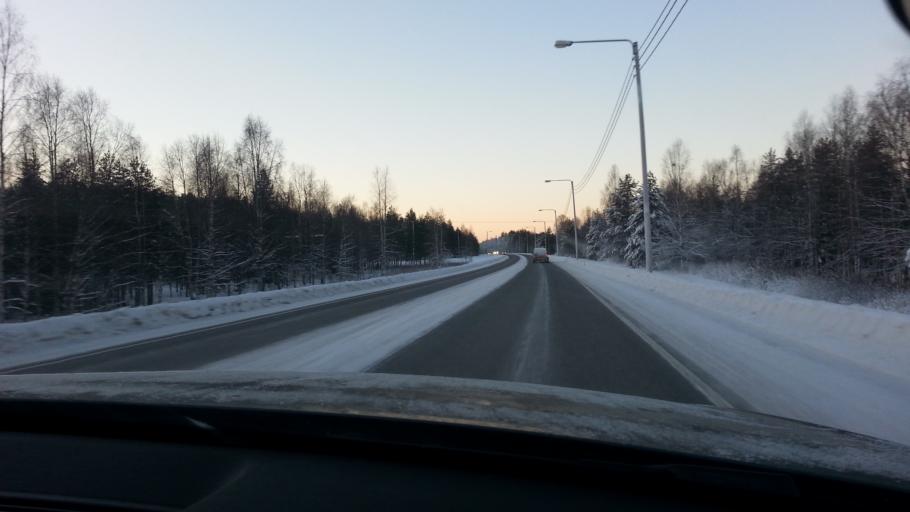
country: FI
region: Lapland
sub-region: Rovaniemi
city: Rovaniemi
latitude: 66.5418
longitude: 25.8066
